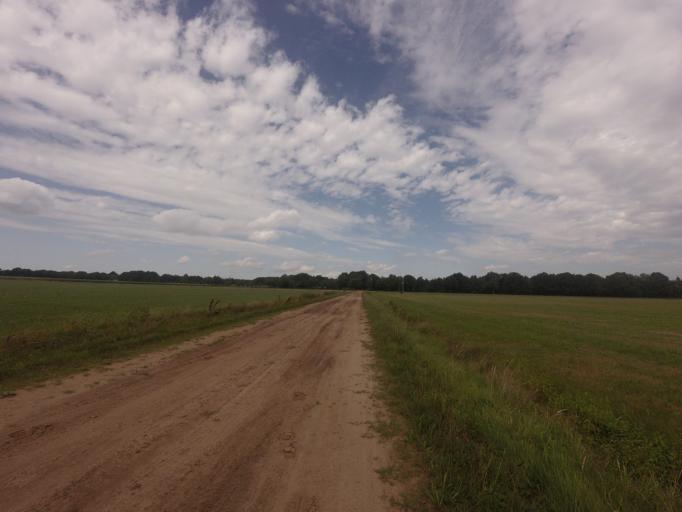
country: NL
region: Overijssel
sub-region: Gemeente Twenterand
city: Den Ham
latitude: 52.4828
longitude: 6.3757
